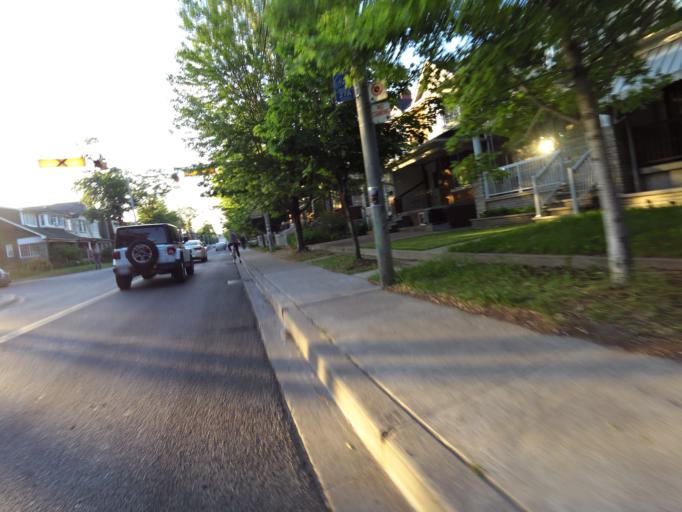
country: CA
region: Ontario
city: Toronto
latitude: 43.6536
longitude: -79.4410
